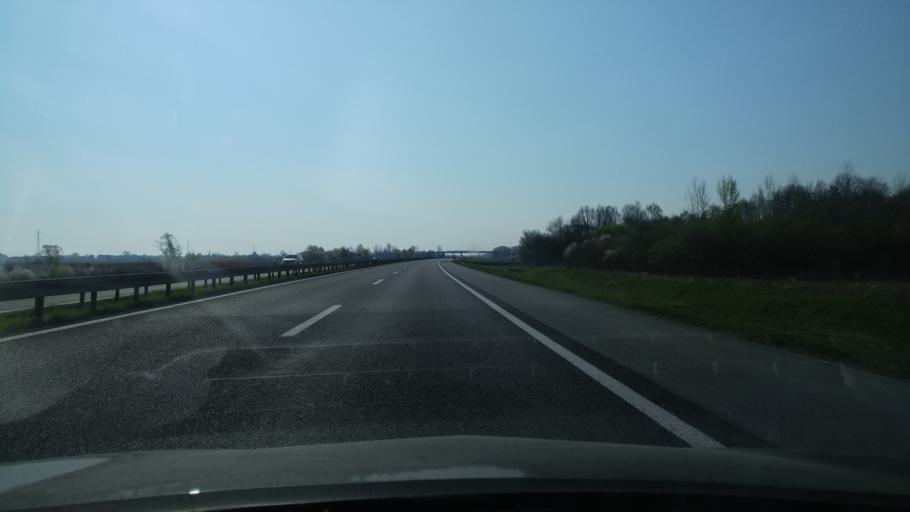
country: HR
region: Sisacko-Moslavacka
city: Osekovo
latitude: 45.5158
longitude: 16.6516
